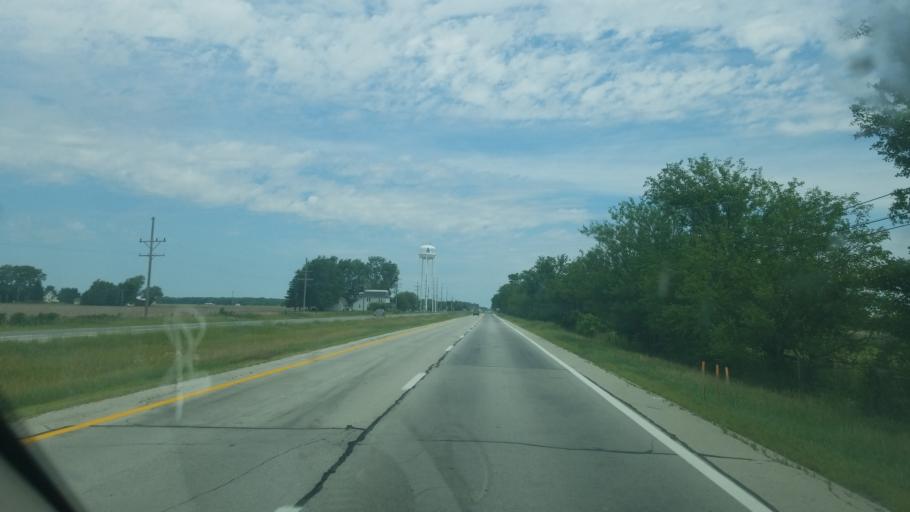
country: US
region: Ohio
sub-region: Wood County
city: North Baltimore
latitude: 41.2647
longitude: -83.6500
